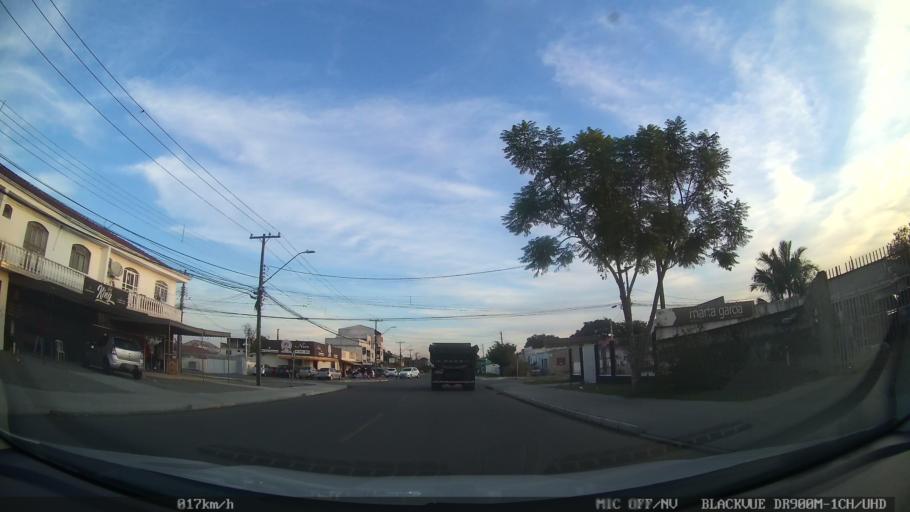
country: BR
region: Parana
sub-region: Pinhais
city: Pinhais
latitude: -25.4610
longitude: -49.1855
